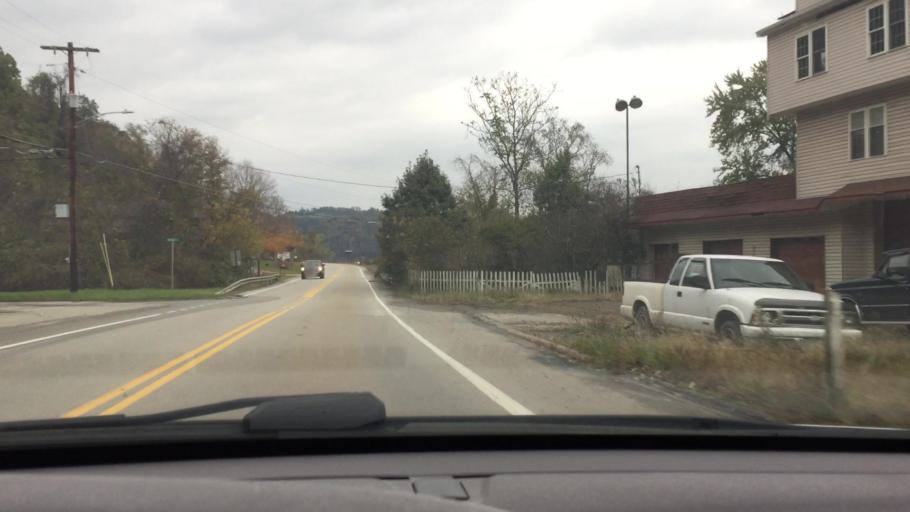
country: US
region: Pennsylvania
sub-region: Fayette County
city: Fairhope
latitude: 40.1006
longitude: -79.8456
